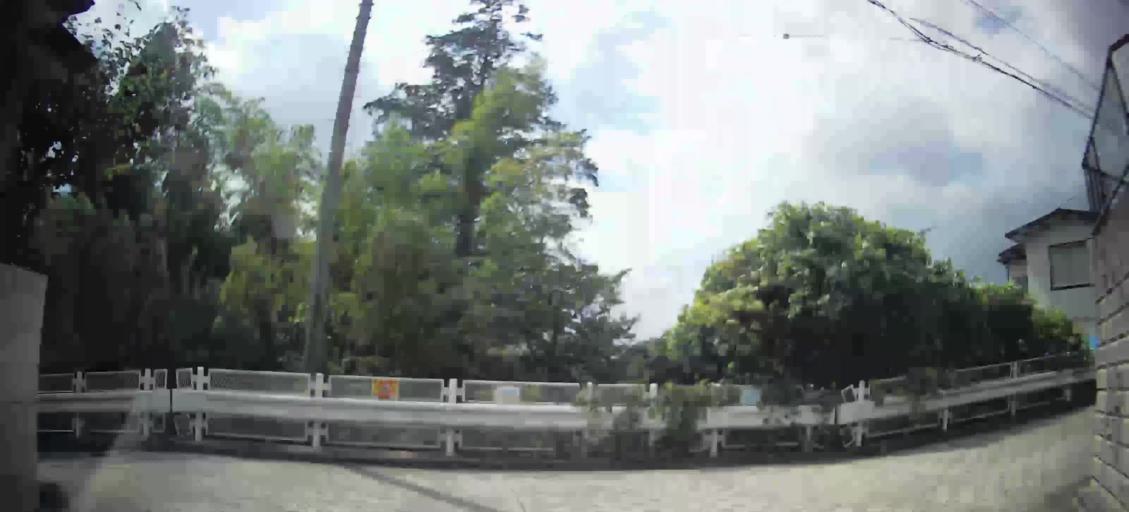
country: JP
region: Kanagawa
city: Yokohama
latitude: 35.4805
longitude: 139.5546
